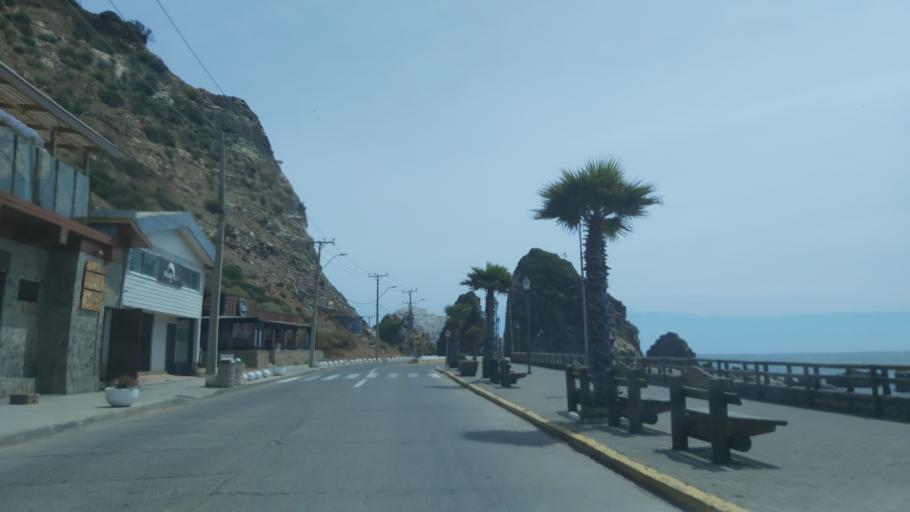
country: CL
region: Maule
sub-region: Provincia de Talca
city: Constitucion
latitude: -35.3262
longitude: -72.4273
